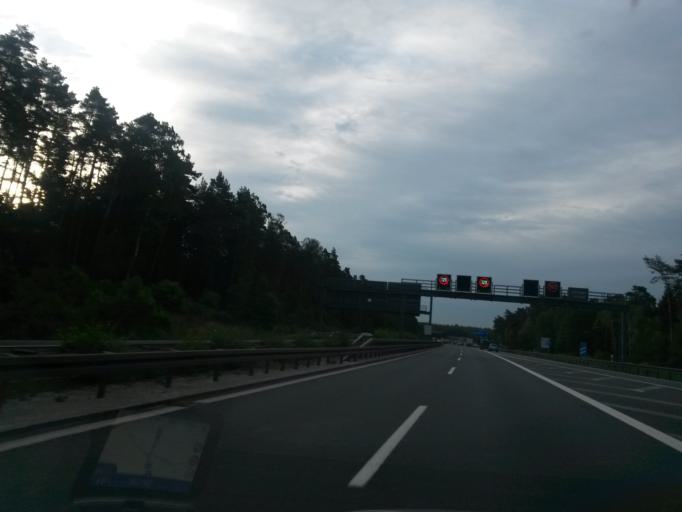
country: DE
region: Bavaria
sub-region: Regierungsbezirk Mittelfranken
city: Wendelstein
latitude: 49.3746
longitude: 11.1439
